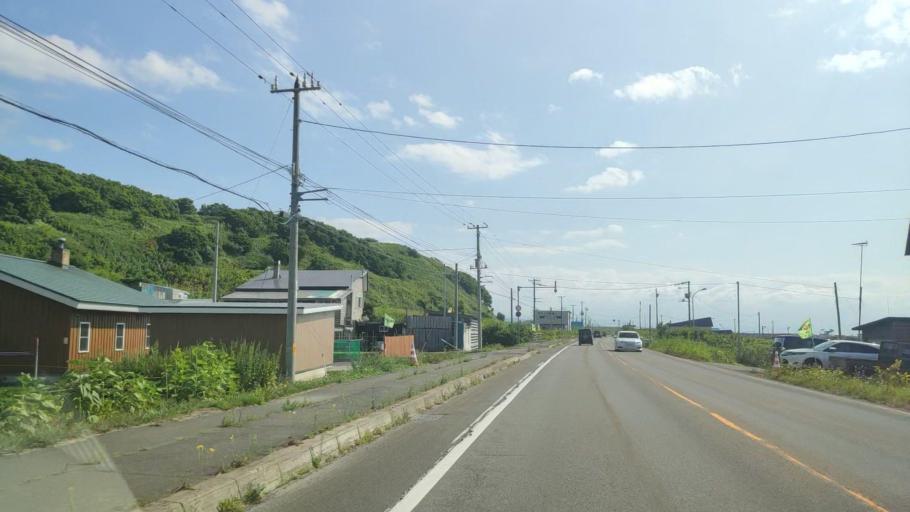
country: JP
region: Hokkaido
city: Rumoi
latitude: 43.9830
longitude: 141.6478
